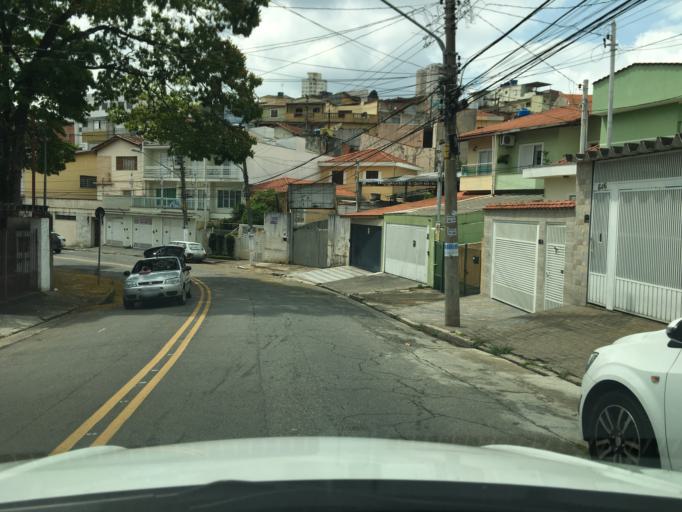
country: BR
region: Sao Paulo
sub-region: Sao Paulo
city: Sao Paulo
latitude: -23.4847
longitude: -46.6474
